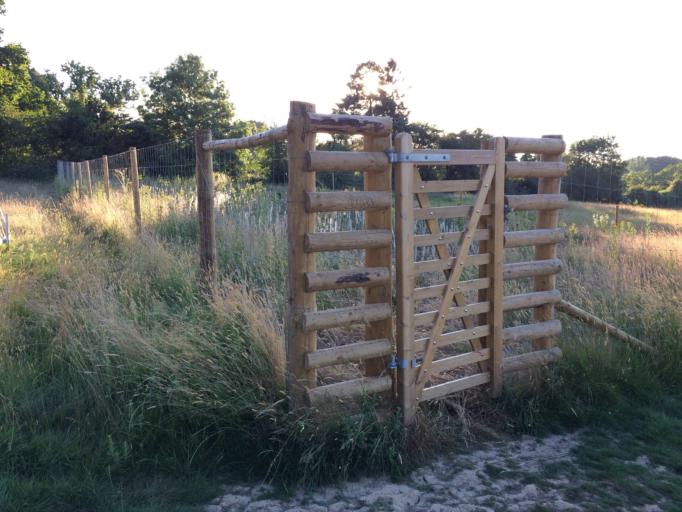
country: GB
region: England
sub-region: East Sussex
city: Newick
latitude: 50.9714
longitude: 0.0047
